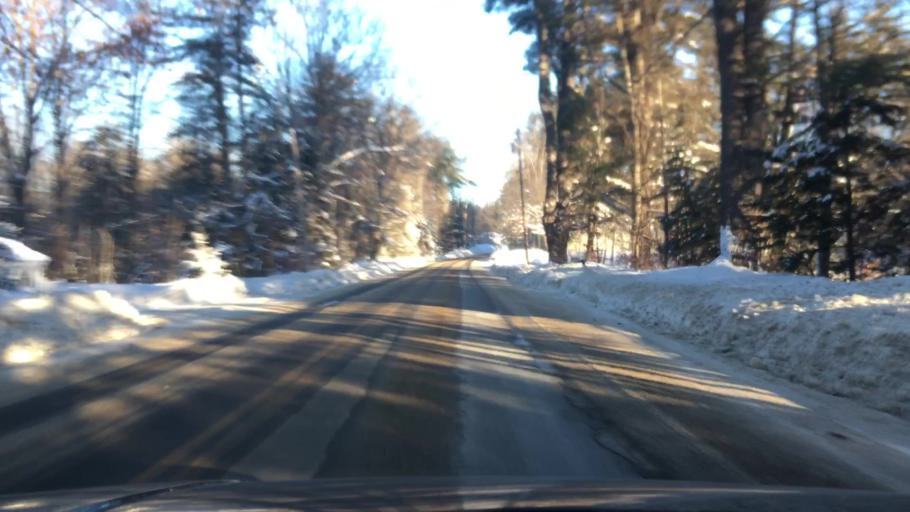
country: US
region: Maine
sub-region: Oxford County
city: Lovell
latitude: 44.1330
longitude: -70.9783
